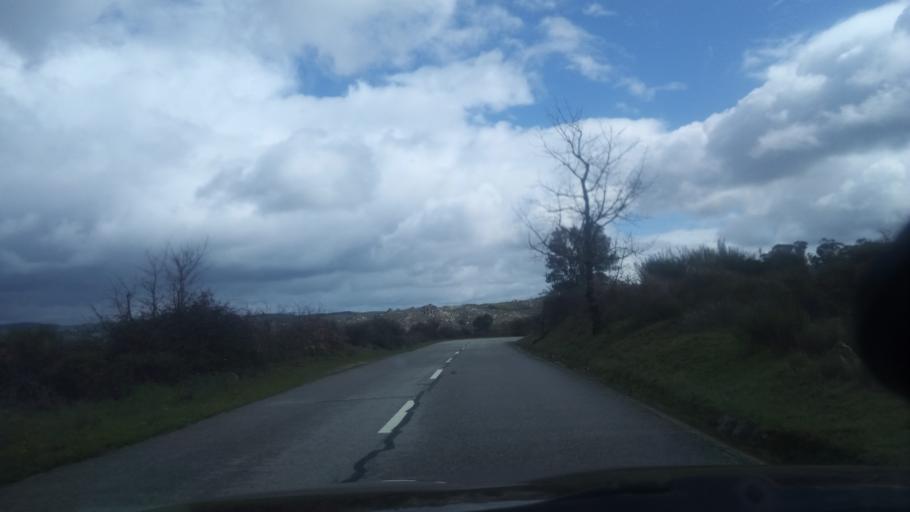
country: PT
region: Guarda
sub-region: Fornos de Algodres
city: Fornos de Algodres
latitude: 40.5944
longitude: -7.4967
